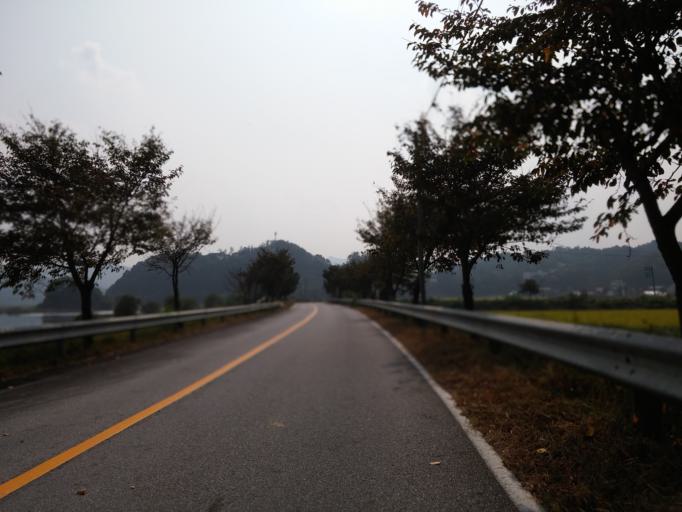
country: KR
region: Chungcheongbuk-do
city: Yong-dong
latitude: 36.3327
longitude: 127.7662
